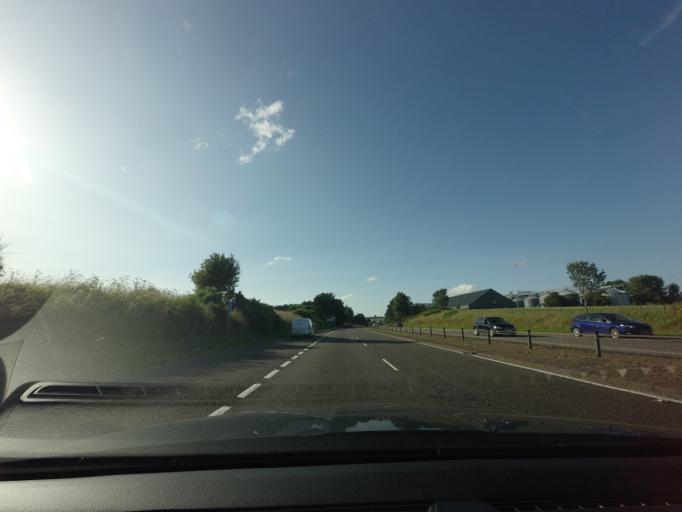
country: GB
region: Scotland
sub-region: Highland
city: Inverness
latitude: 57.5282
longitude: -4.3250
